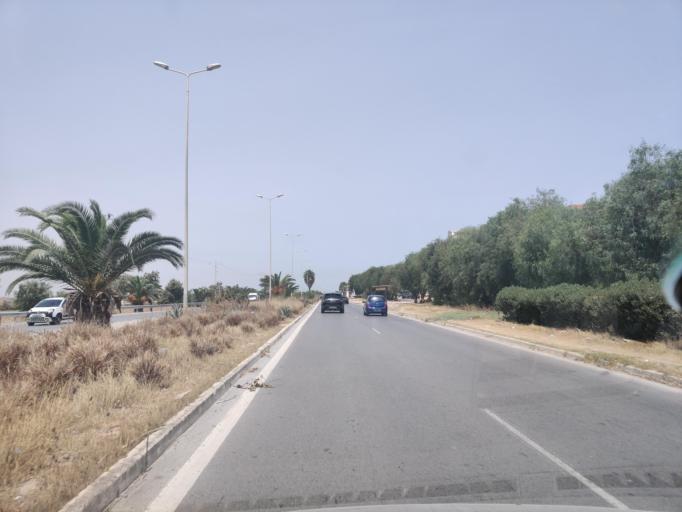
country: TN
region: Tunis
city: Al Marsa
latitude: 36.8928
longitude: 10.2967
